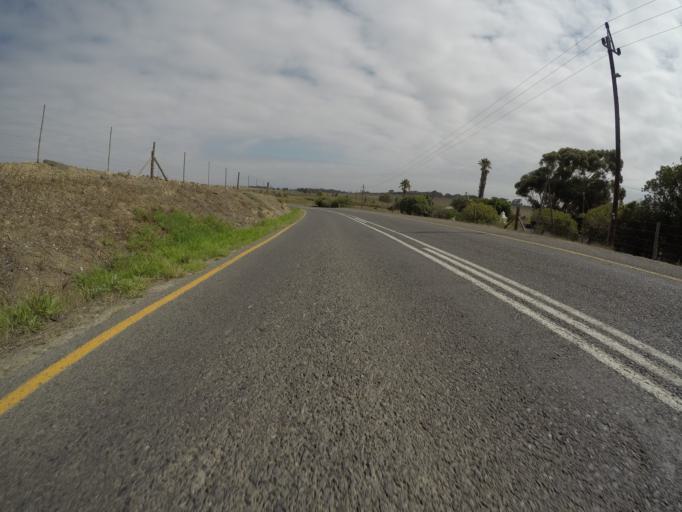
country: ZA
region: Western Cape
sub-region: City of Cape Town
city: Sunset Beach
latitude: -33.7822
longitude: 18.5567
